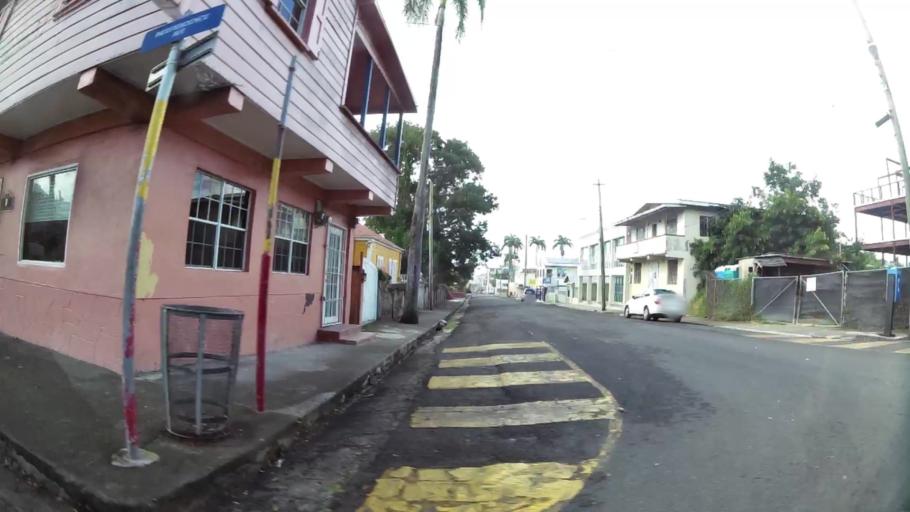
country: AG
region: Saint John
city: Saint John's
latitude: 17.1200
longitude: -61.8401
